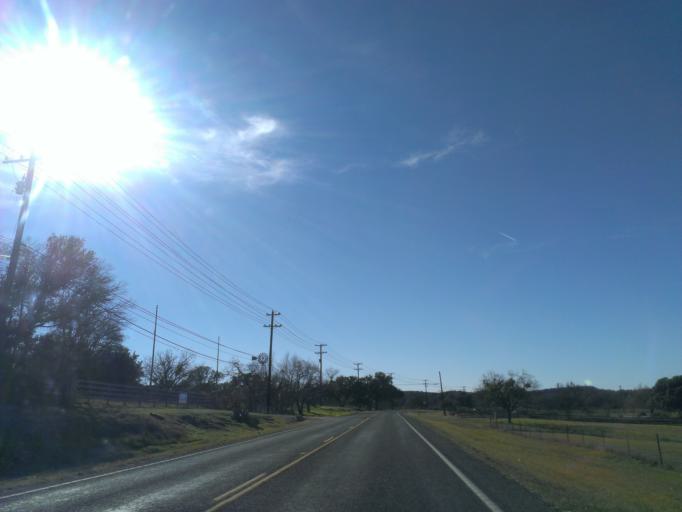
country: US
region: Texas
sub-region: Burnet County
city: Meadowlakes
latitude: 30.5454
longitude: -98.3024
